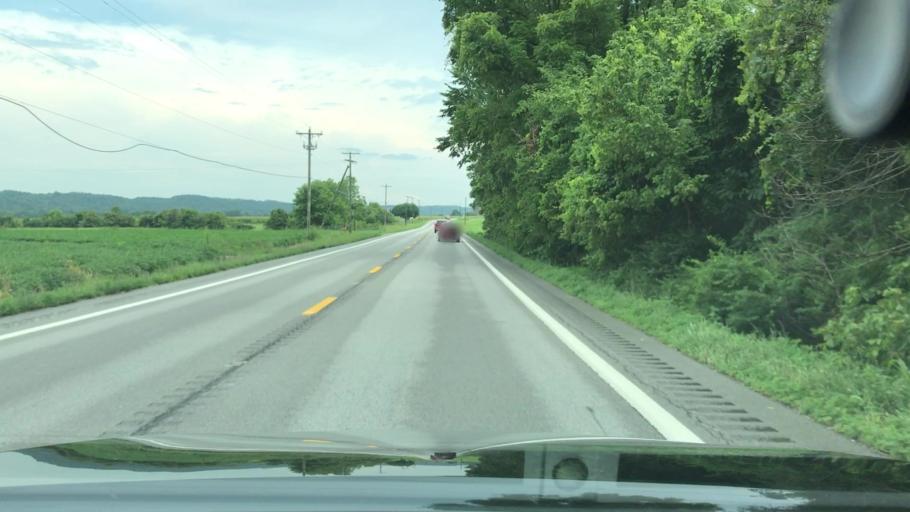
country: US
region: West Virginia
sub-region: Putnam County
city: Buffalo
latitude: 38.7429
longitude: -81.9795
